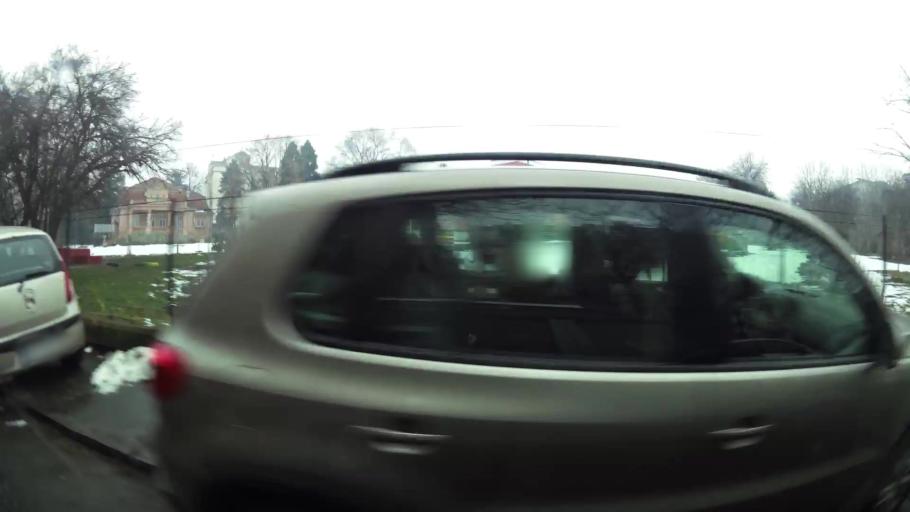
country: RS
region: Central Serbia
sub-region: Belgrade
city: Cukarica
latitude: 44.7837
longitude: 20.4199
